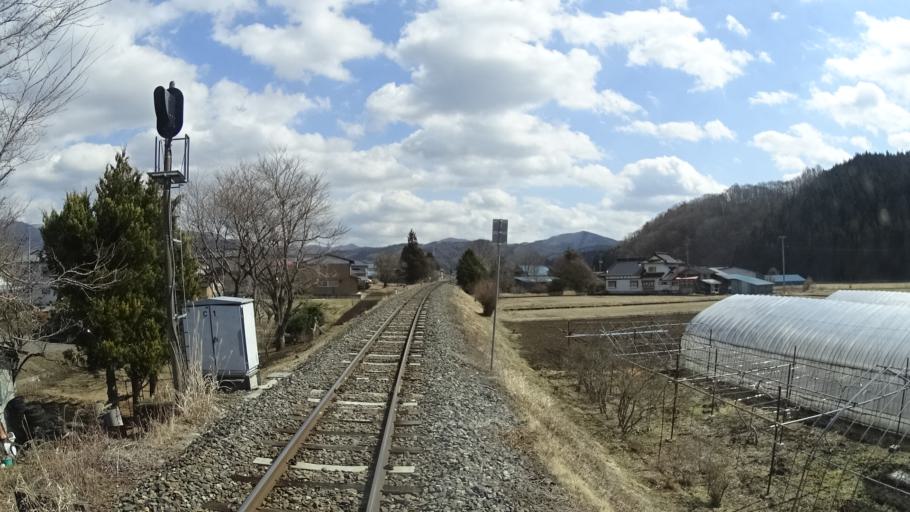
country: JP
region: Iwate
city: Tono
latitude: 39.2867
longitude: 141.5837
